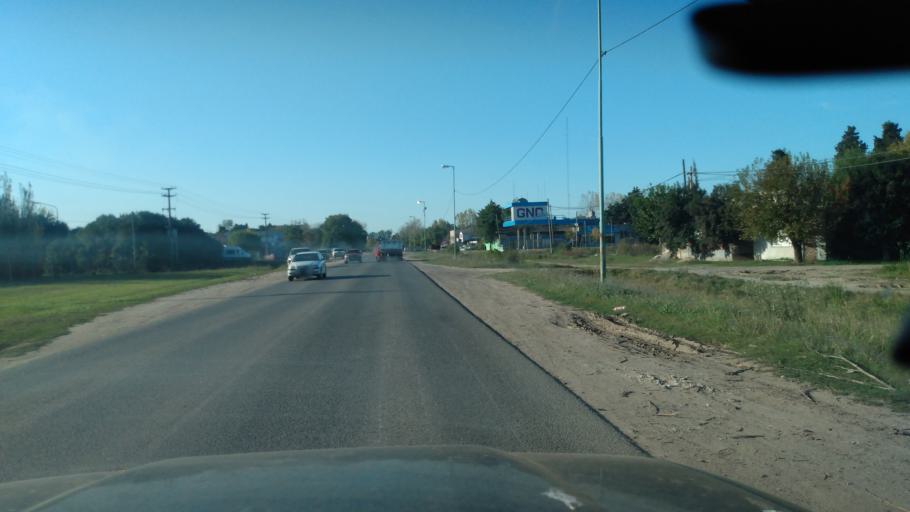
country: AR
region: Buenos Aires
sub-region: Partido de Lujan
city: Lujan
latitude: -34.5417
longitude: -59.1209
